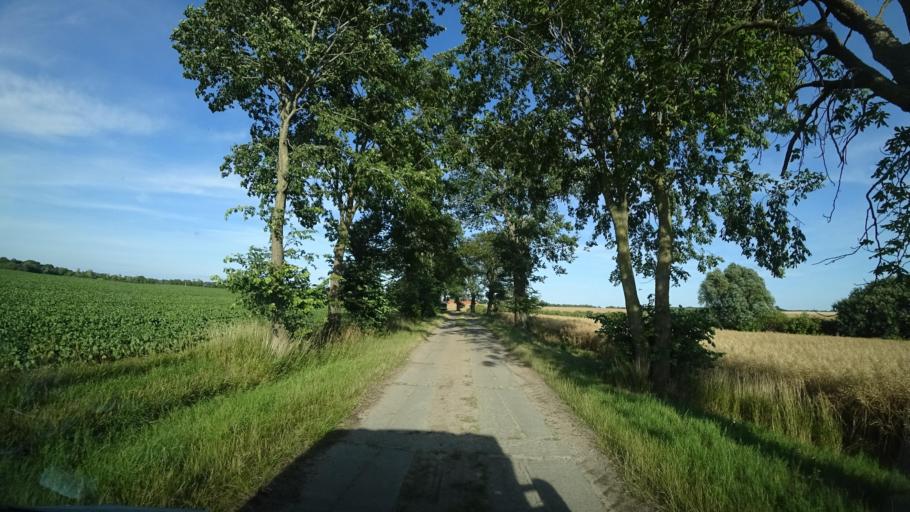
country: DE
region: Mecklenburg-Vorpommern
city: Rambin
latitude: 54.3226
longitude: 13.1886
